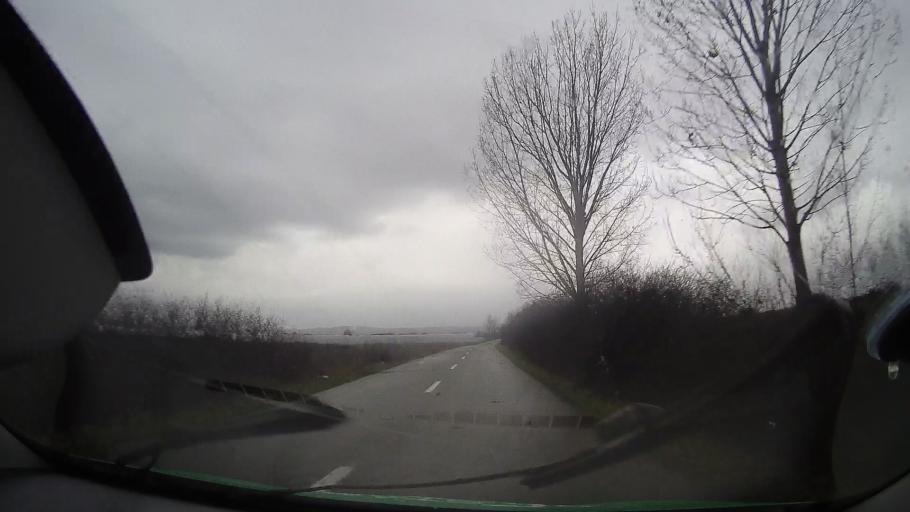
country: RO
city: Capalna
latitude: 46.7243
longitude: 22.0878
